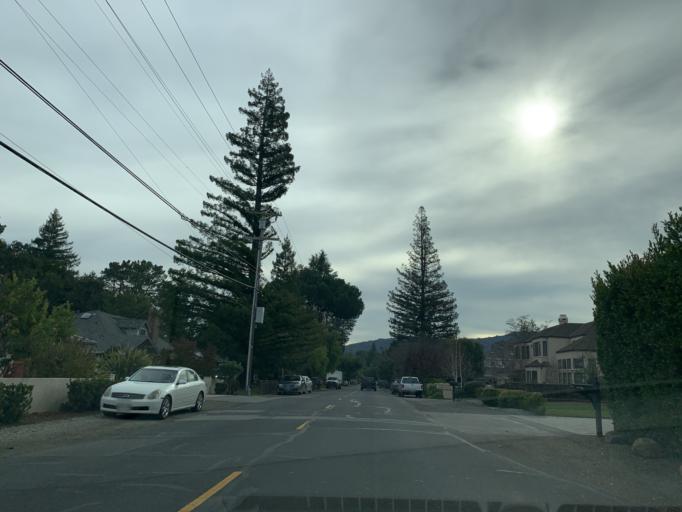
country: US
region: California
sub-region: Santa Clara County
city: Loyola
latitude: 37.3684
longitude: -122.1020
